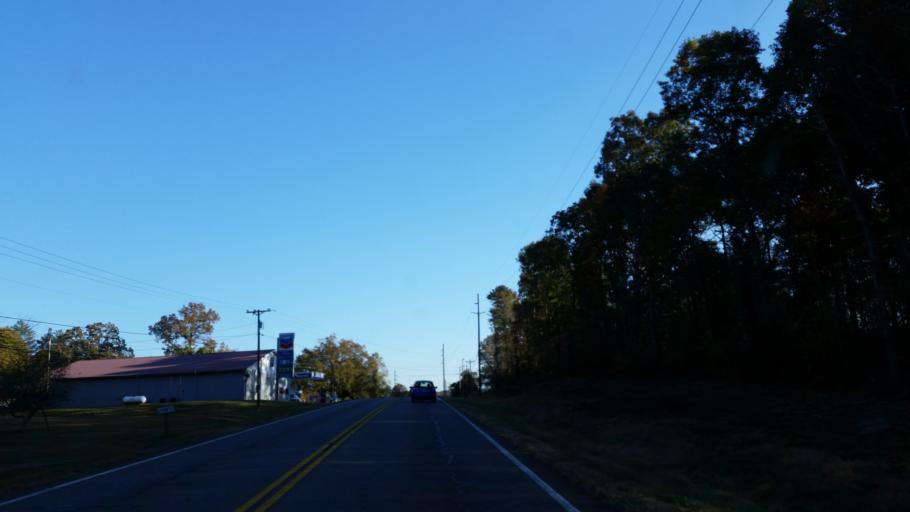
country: US
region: Georgia
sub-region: Gilmer County
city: Ellijay
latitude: 34.6459
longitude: -84.3913
